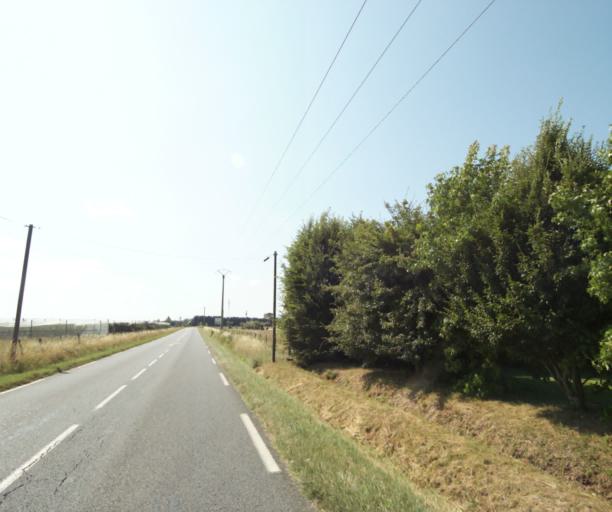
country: FR
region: Centre
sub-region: Departement du Loiret
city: Saint-Cyr-en-Val
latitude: 47.8475
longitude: 1.9565
